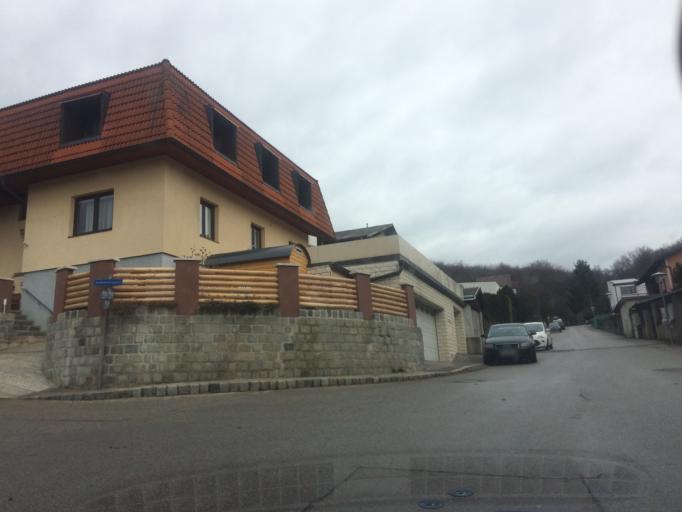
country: AT
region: Lower Austria
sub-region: Politischer Bezirk Wien-Umgebung
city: Gablitz
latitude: 48.2329
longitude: 16.1514
